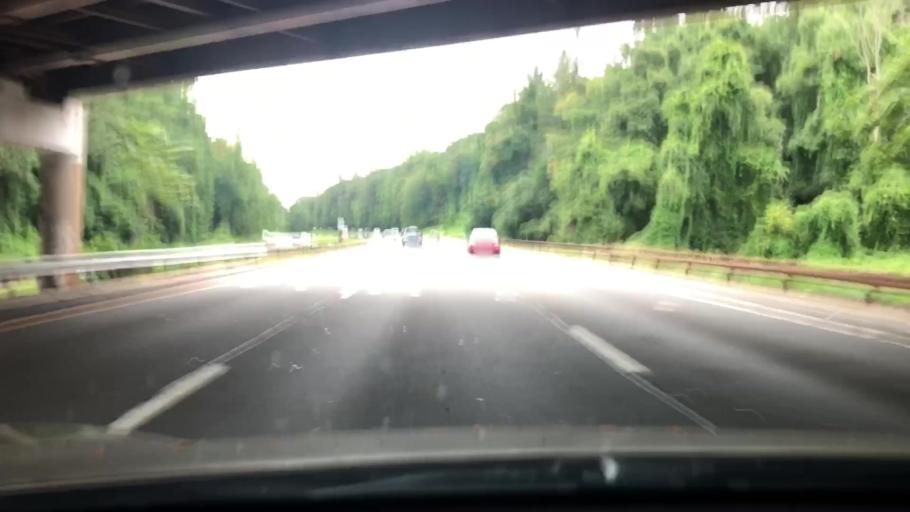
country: US
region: New York
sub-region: Westchester County
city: Greenville
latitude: 40.9995
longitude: -73.8315
